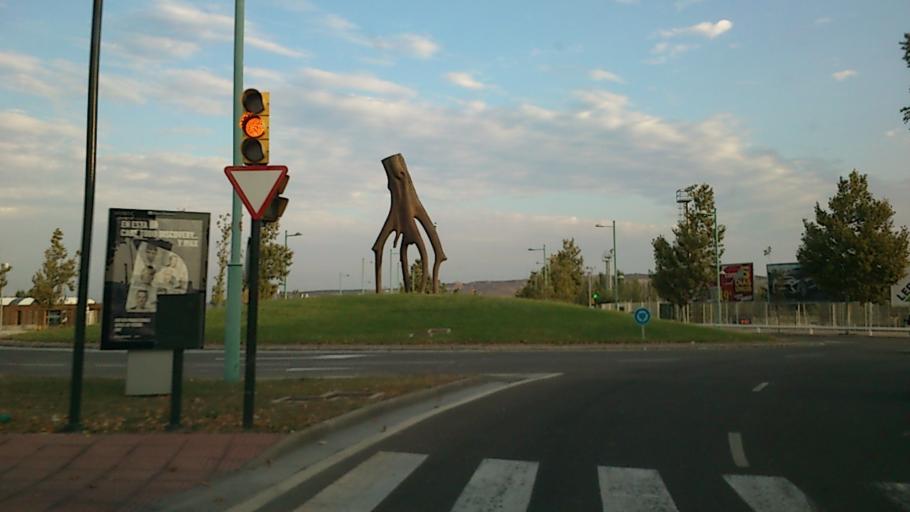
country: ES
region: Aragon
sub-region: Provincia de Zaragoza
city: Almozara
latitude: 41.6755
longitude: -0.8983
